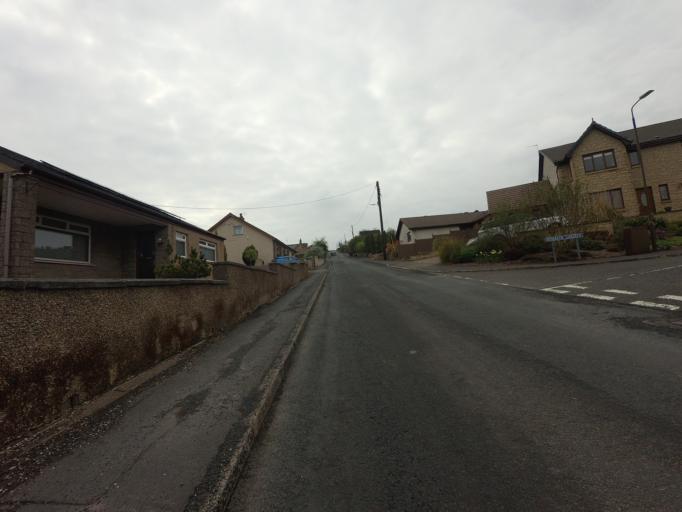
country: GB
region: Scotland
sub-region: Falkirk
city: Polmont
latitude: 55.9774
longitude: -3.7363
